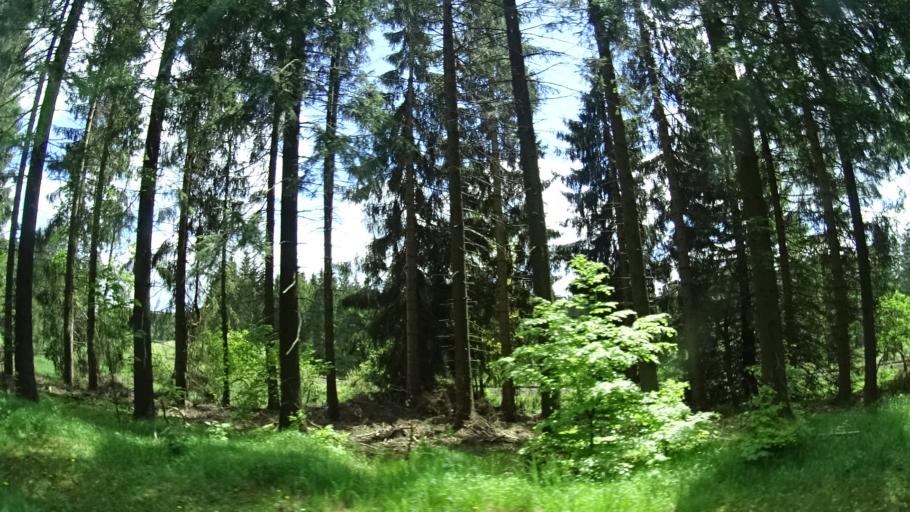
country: DE
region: Thuringia
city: Schmiedefeld am Rennsteig
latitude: 50.6155
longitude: 10.8291
